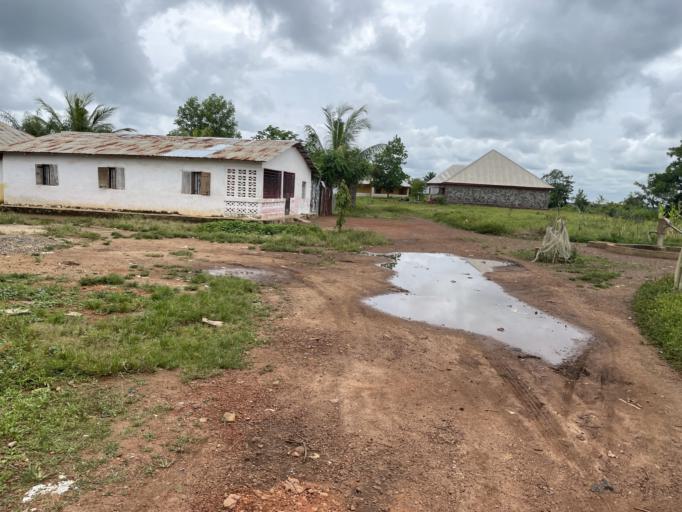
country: SL
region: Northern Province
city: Kambia
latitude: 9.1260
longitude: -12.9058
